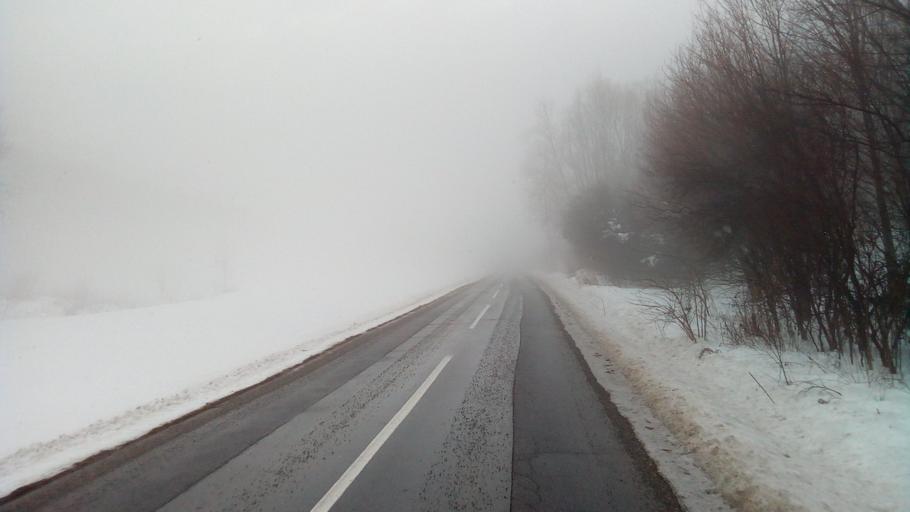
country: HR
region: Sisacko-Moslavacka
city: Petrinja
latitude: 45.3677
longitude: 16.2785
